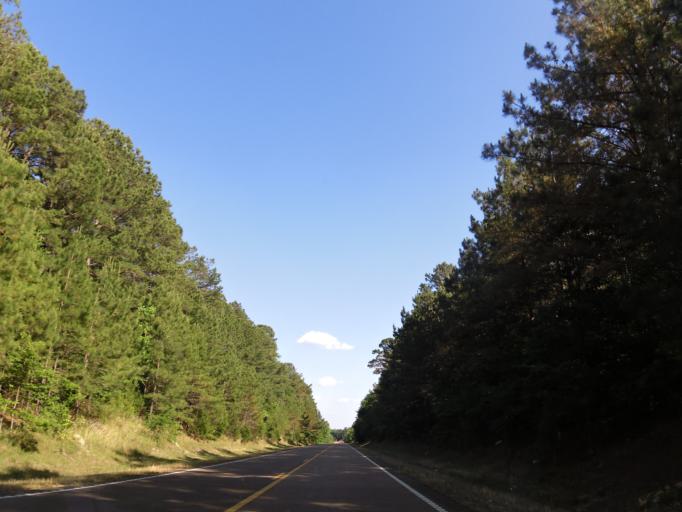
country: US
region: Mississippi
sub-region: Yalobusha County
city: Water Valley
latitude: 34.1861
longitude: -89.4657
